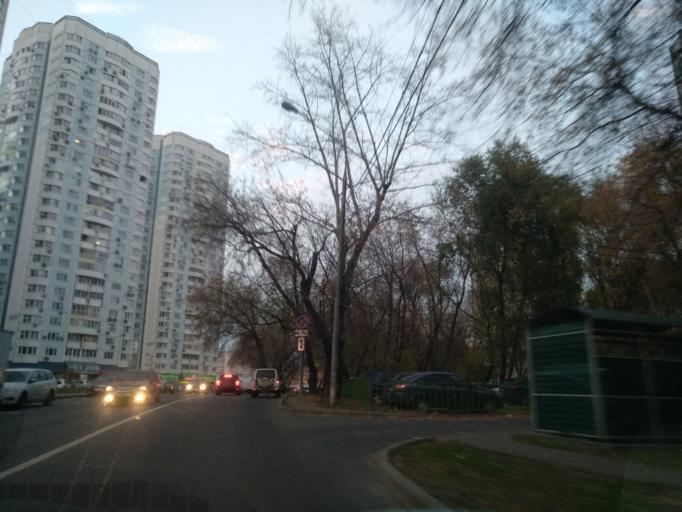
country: RU
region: Moscow
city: Sviblovo
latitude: 55.8676
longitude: 37.6401
